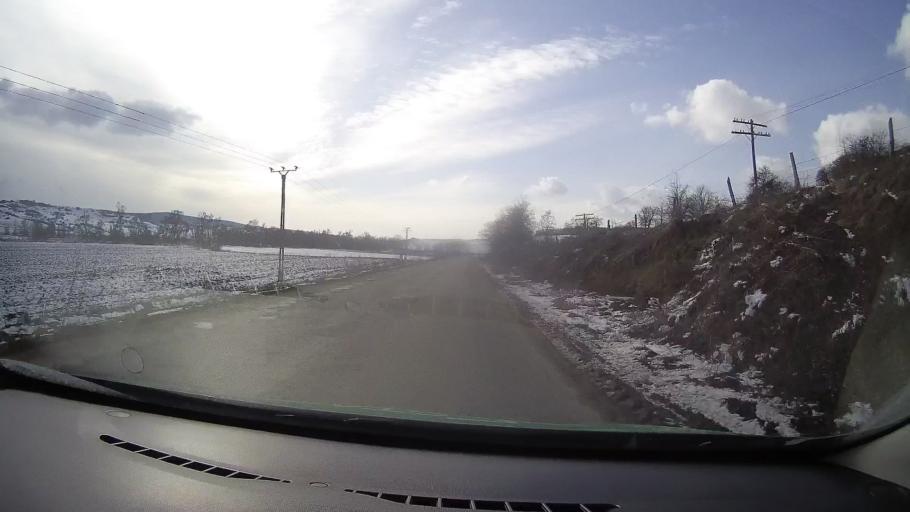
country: RO
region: Sibiu
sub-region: Comuna Iacobeni
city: Iacobeni
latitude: 46.0505
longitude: 24.7726
